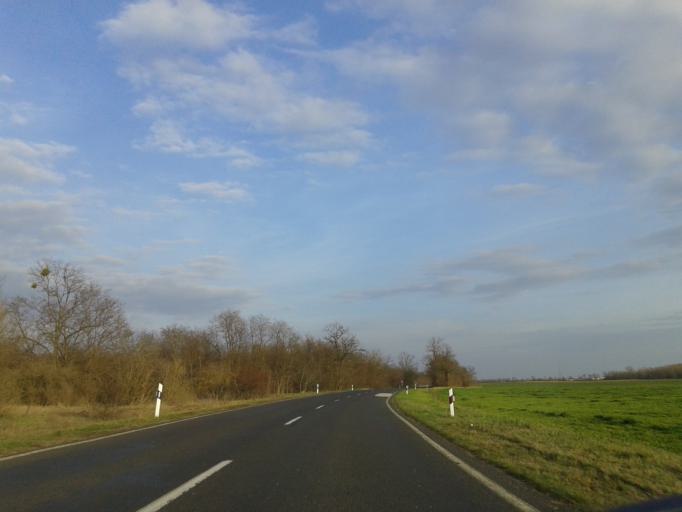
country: HU
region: Komarom-Esztergom
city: Acs
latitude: 47.7392
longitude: 17.9620
